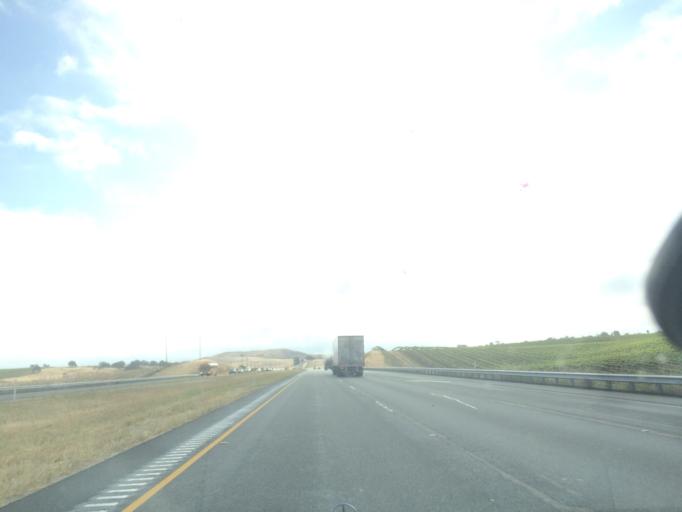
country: US
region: California
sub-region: San Luis Obispo County
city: Paso Robles
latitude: 35.6593
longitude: -120.5568
